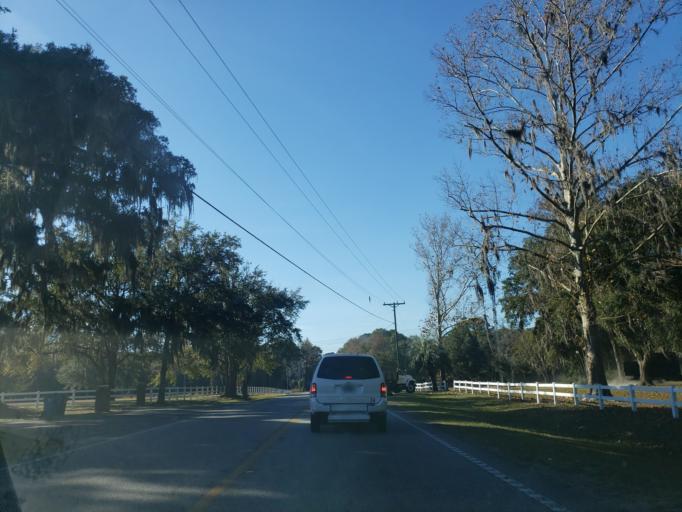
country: US
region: Georgia
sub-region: Glynn County
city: Dock Junction
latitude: 31.2742
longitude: -81.5724
